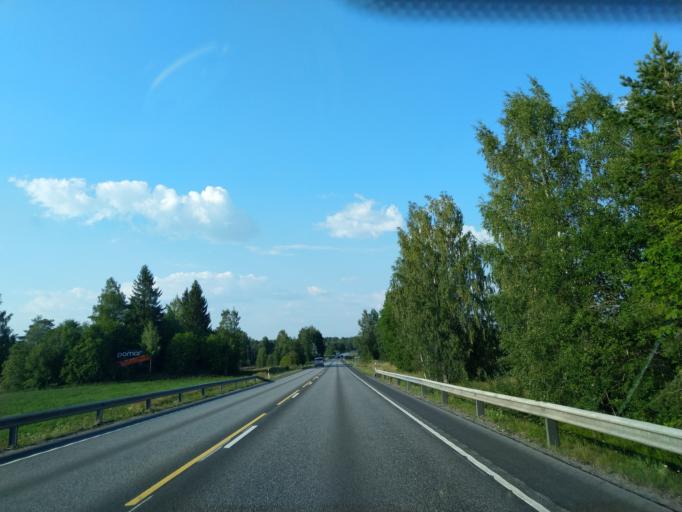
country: FI
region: Satakunta
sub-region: Pori
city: Pomarkku
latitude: 61.6936
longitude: 22.0028
